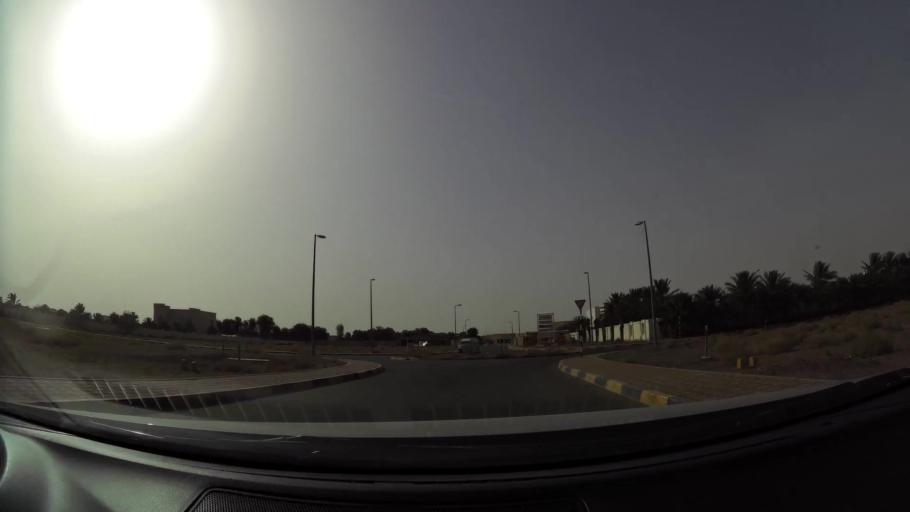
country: AE
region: Abu Dhabi
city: Al Ain
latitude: 24.1896
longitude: 55.6083
